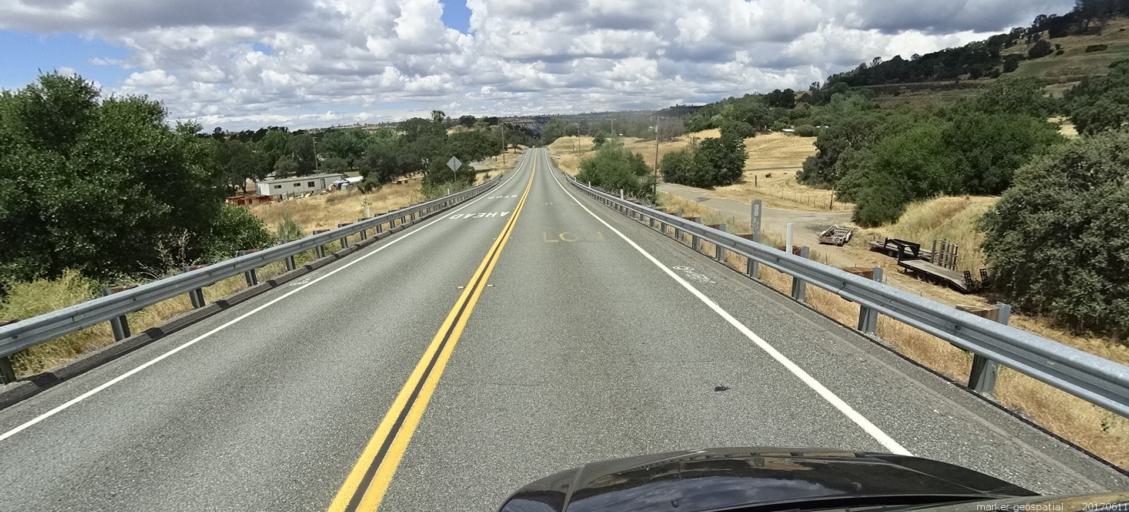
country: US
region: California
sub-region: Butte County
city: Paradise
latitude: 39.6506
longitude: -121.5604
